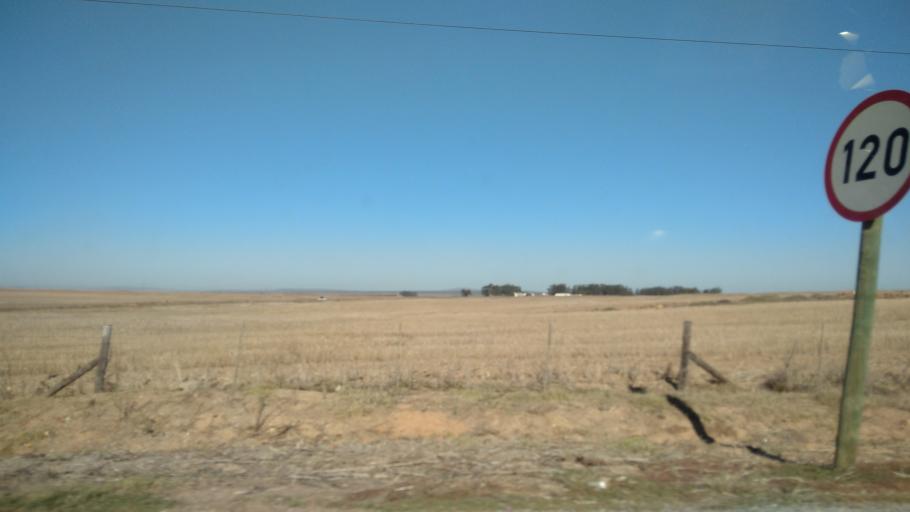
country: ZA
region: Western Cape
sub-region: West Coast District Municipality
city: Moorreesburg
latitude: -33.1352
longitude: 18.4542
